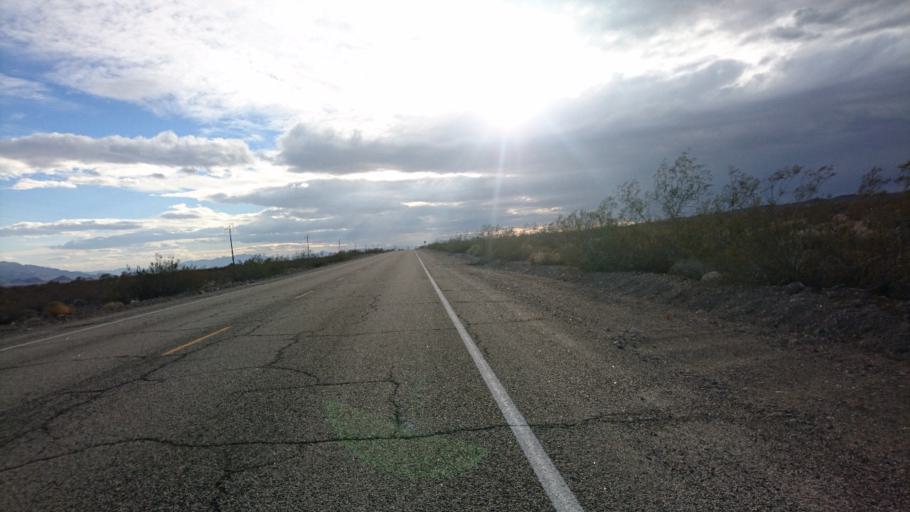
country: US
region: California
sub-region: San Bernardino County
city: Needles
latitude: 34.6699
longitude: -115.3409
